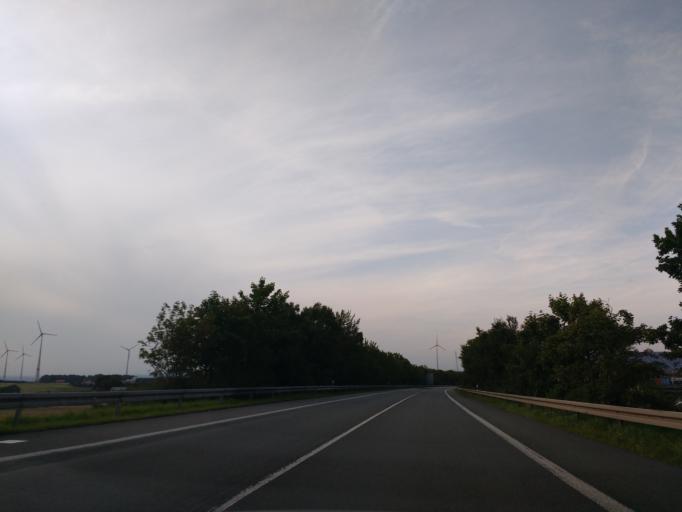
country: DE
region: North Rhine-Westphalia
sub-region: Regierungsbezirk Detmold
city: Wunnenberg
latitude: 51.5673
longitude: 8.7136
